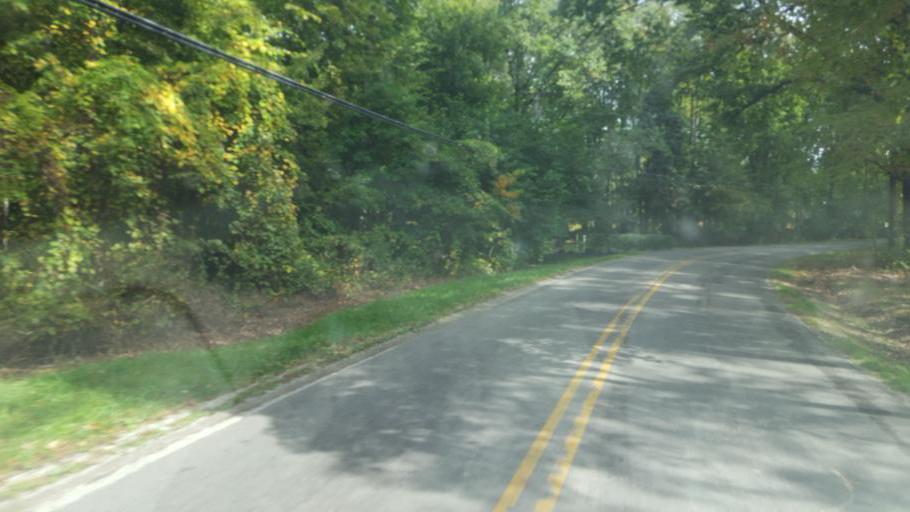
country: US
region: Ohio
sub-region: Lorain County
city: Vermilion
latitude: 41.3865
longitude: -82.3738
